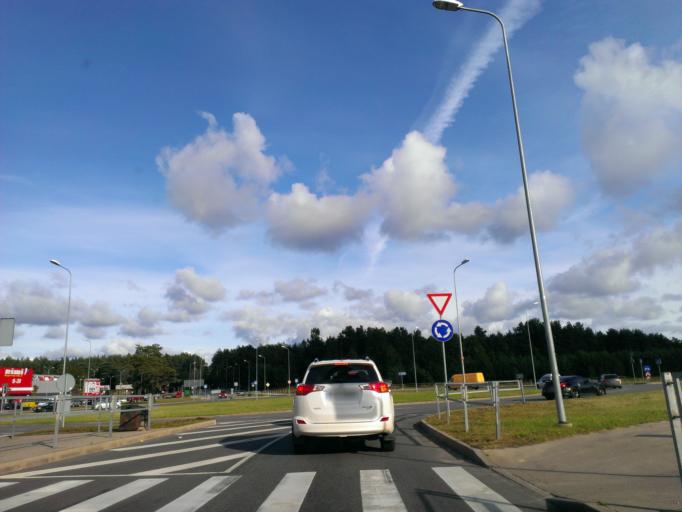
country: LV
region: Stopini
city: Ulbroka
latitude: 56.9563
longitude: 24.2515
